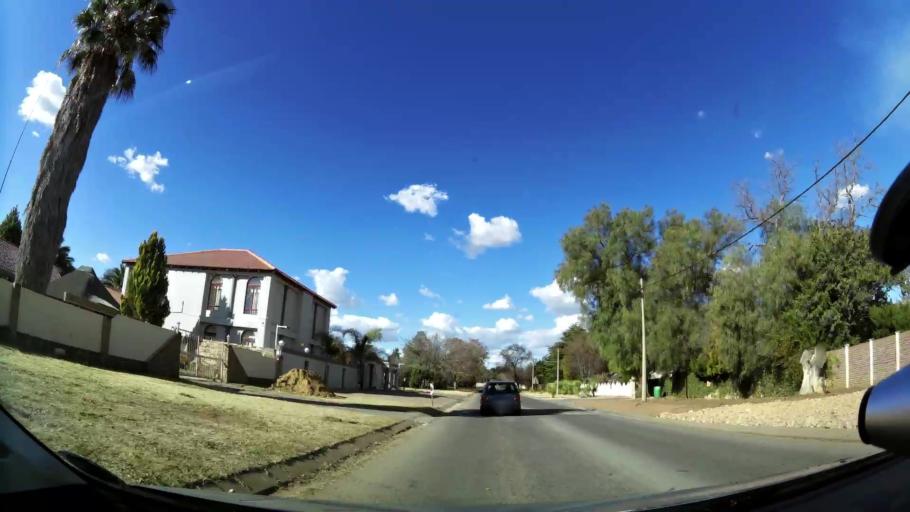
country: ZA
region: North-West
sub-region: Dr Kenneth Kaunda District Municipality
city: Klerksdorp
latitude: -26.8246
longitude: 26.6644
